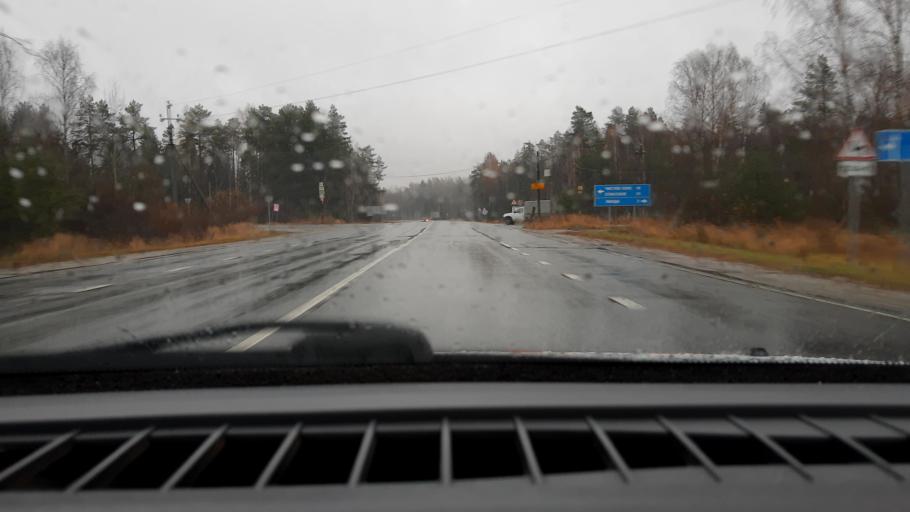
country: RU
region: Nizjnij Novgorod
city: Linda
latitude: 56.6341
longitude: 44.0982
